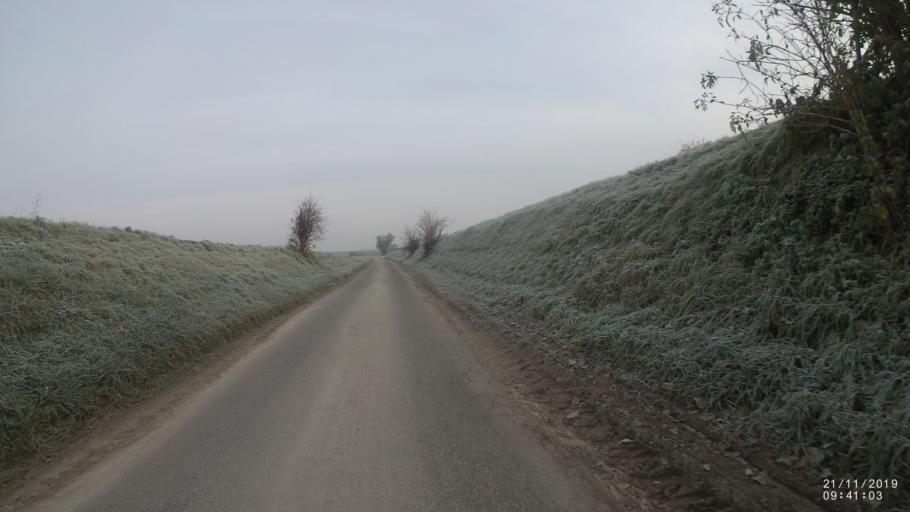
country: BE
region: Flanders
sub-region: Provincie Vlaams-Brabant
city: Tienen
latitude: 50.7774
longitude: 4.9938
